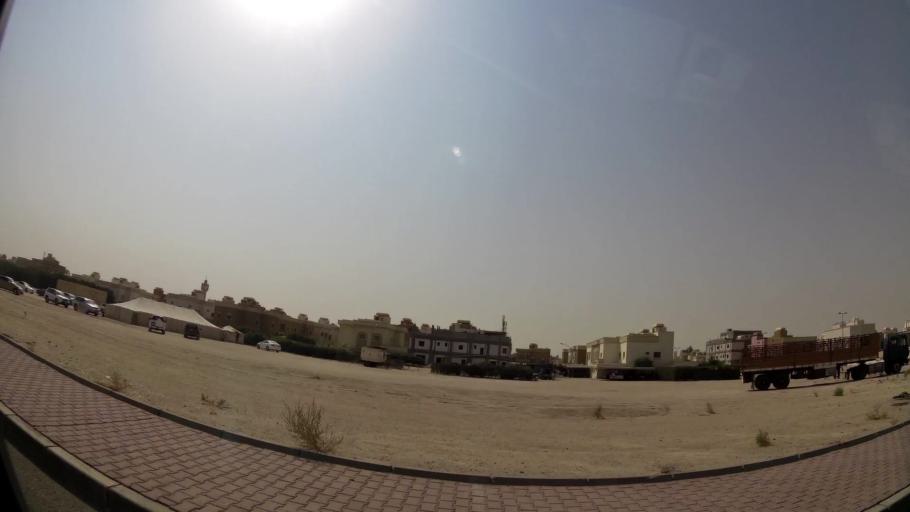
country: KW
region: Muhafazat al Jahra'
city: Al Jahra'
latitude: 29.3250
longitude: 47.7254
